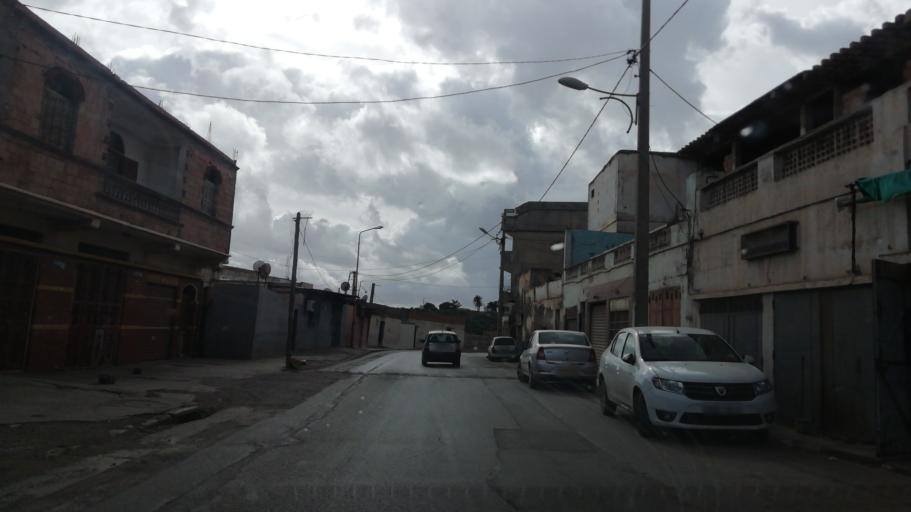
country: DZ
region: Oran
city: Oran
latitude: 35.6987
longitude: -0.6596
